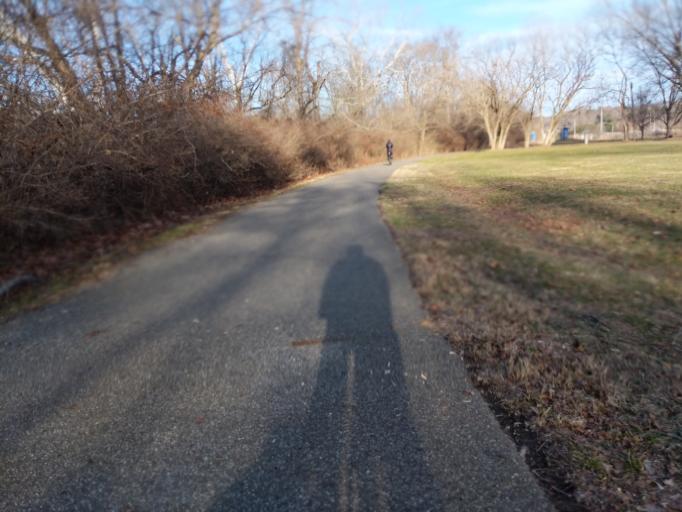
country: US
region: Ohio
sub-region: Athens County
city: Athens
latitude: 39.3360
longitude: -82.1236
